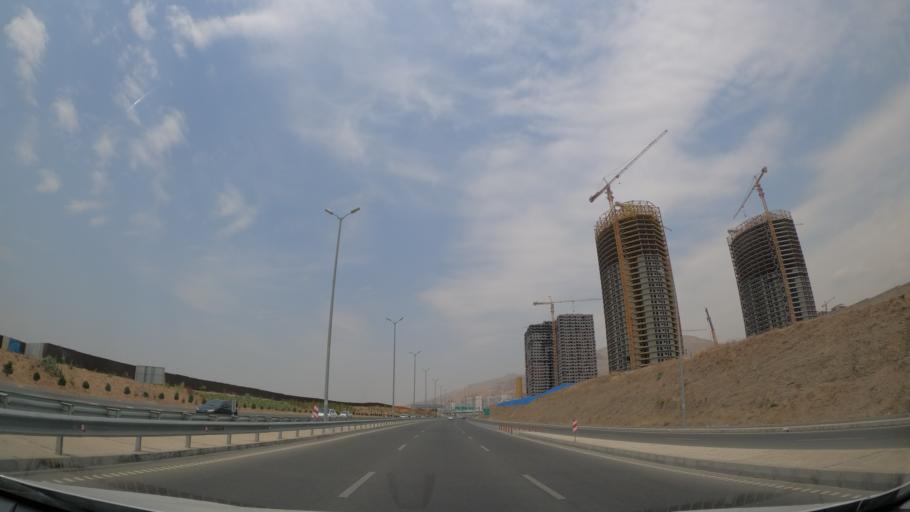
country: IR
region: Tehran
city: Shahr-e Qods
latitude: 35.7471
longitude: 51.1814
